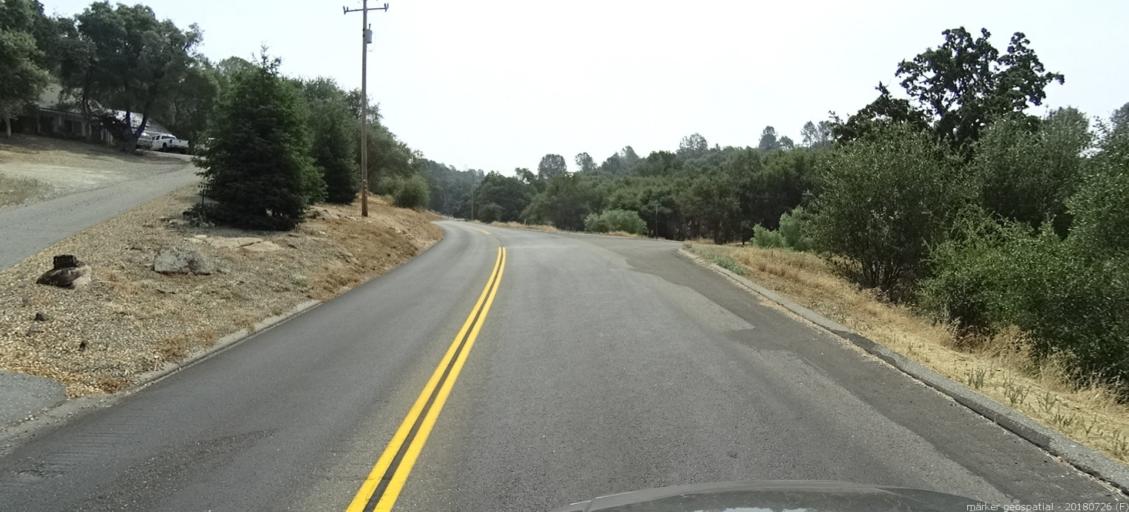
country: US
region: California
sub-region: Madera County
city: Coarsegold
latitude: 37.2477
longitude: -119.6921
